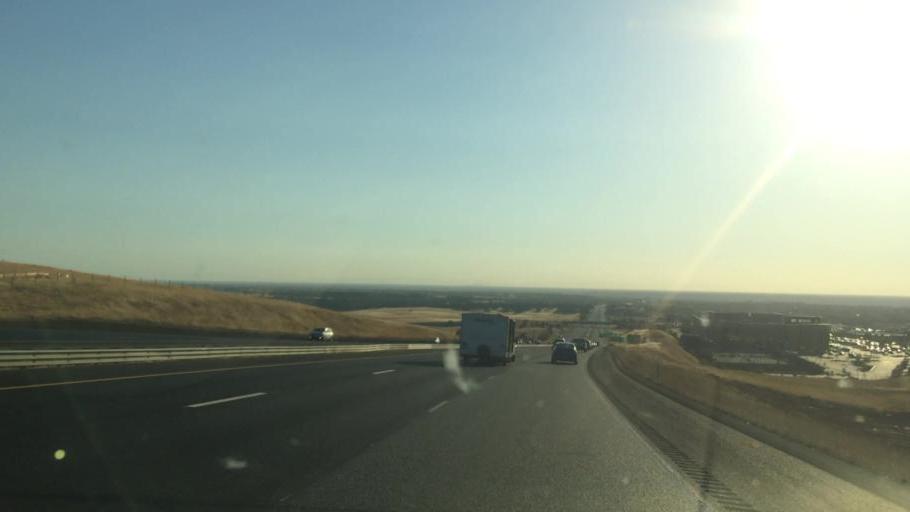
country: US
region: California
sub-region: El Dorado County
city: El Dorado Hills
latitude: 38.6442
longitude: -121.0984
